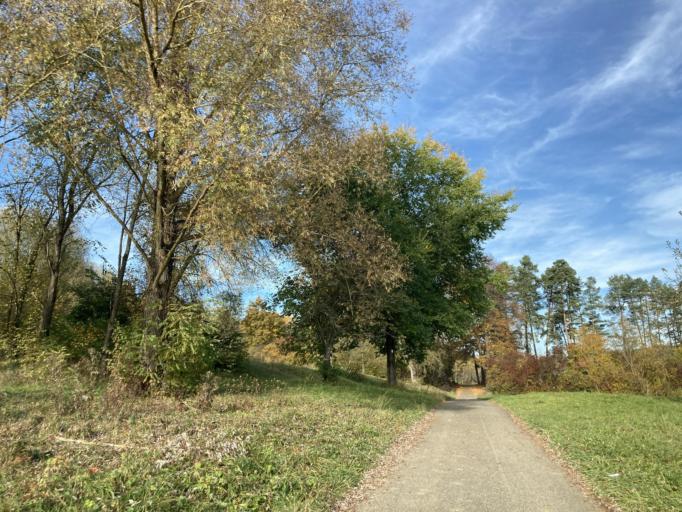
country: DE
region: Baden-Wuerttemberg
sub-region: Tuebingen Region
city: Bodelshausen
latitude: 48.4002
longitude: 8.9651
